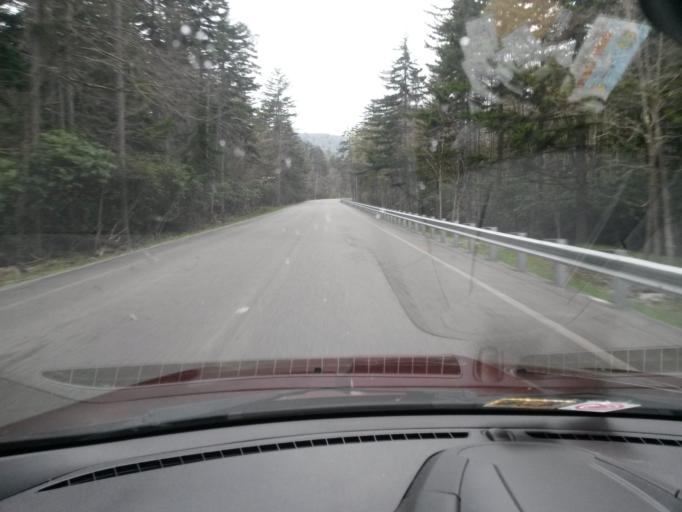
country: US
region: West Virginia
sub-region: Randolph County
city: Elkins
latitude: 38.6260
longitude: -79.8860
